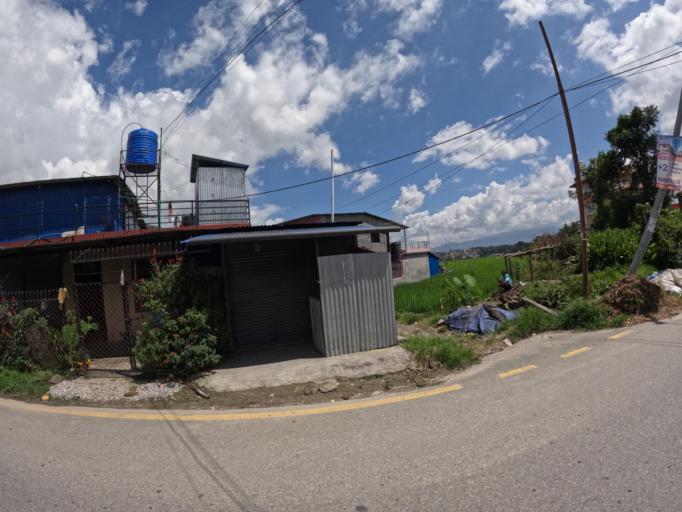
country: NP
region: Central Region
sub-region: Bagmati Zone
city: Kathmandu
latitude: 27.7829
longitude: 85.3254
